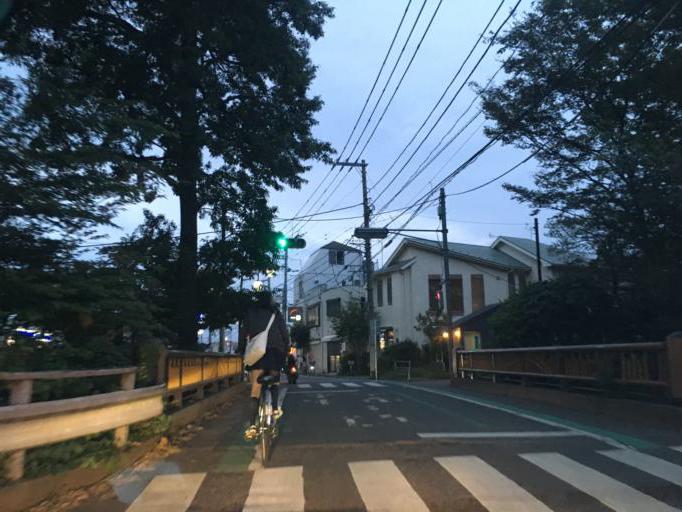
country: JP
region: Tokyo
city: Kokubunji
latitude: 35.7224
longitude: 139.4572
